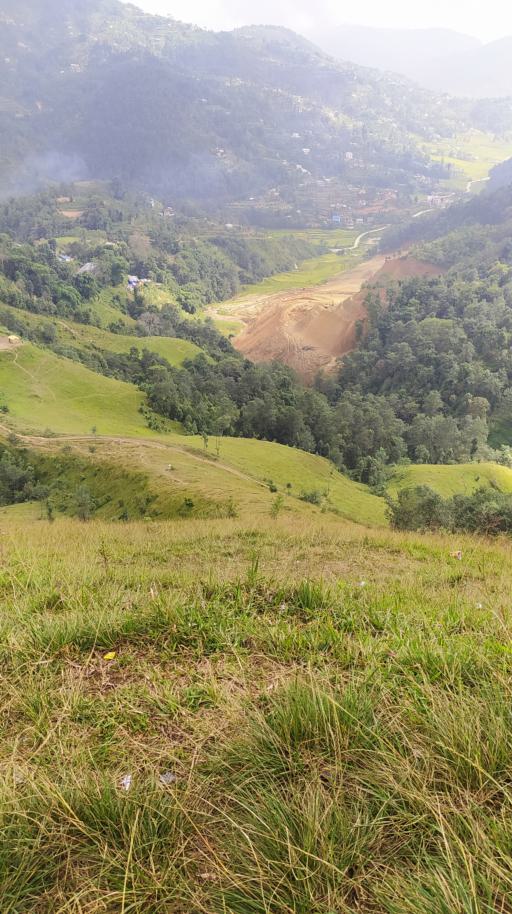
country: NP
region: Central Region
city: Panaoti
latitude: 27.5996
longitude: 85.4912
